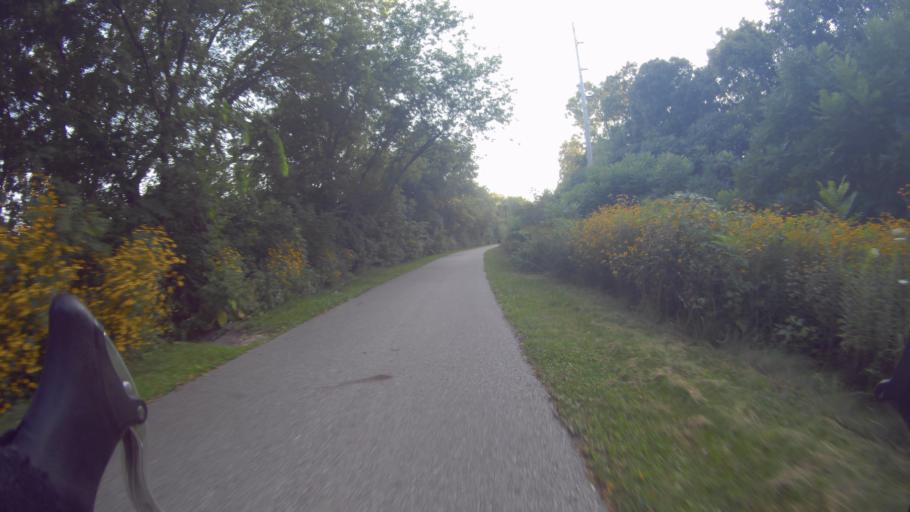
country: US
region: Wisconsin
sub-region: Dane County
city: Madison
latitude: 43.0248
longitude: -89.4262
